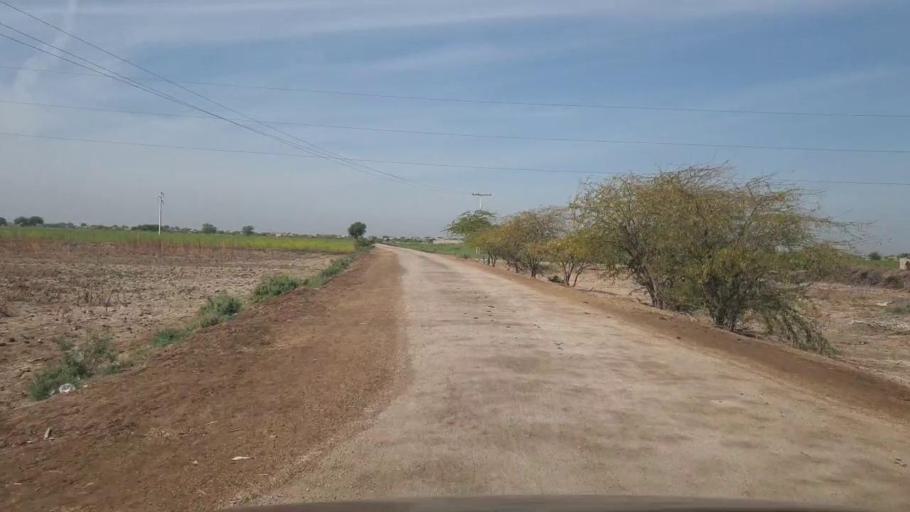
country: PK
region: Sindh
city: Umarkot
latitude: 25.3517
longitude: 69.5962
